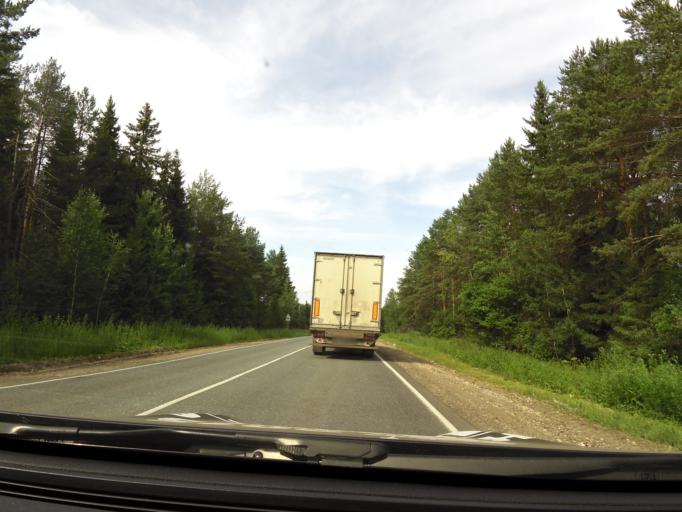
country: RU
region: Kirov
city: Slobodskoy
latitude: 58.7606
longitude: 50.3317
